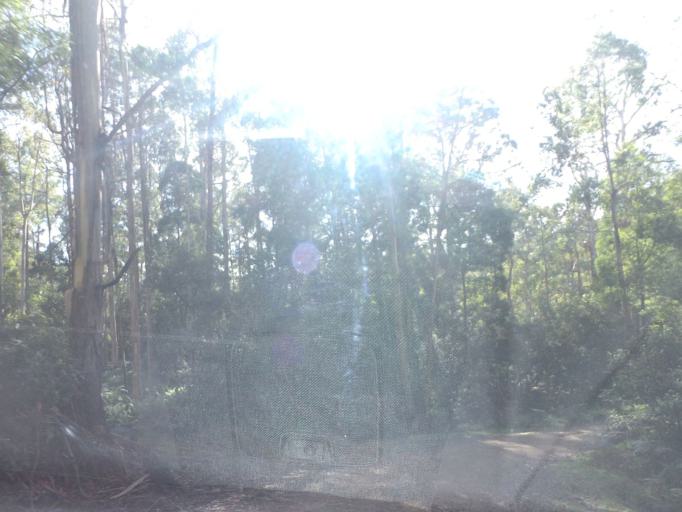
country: AU
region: Victoria
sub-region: Moorabool
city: Bacchus Marsh
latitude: -37.4271
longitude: 144.2369
